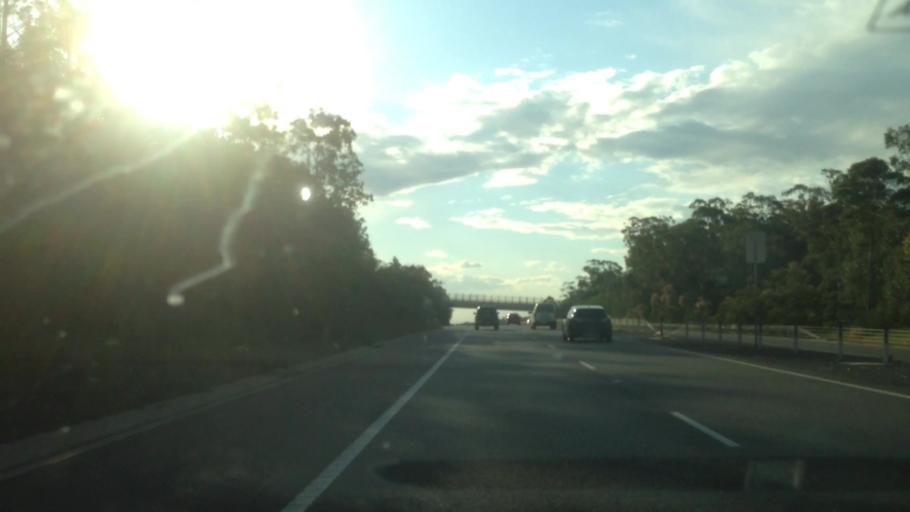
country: AU
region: New South Wales
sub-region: Lake Macquarie Shire
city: Holmesville
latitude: -32.8842
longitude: 151.5911
